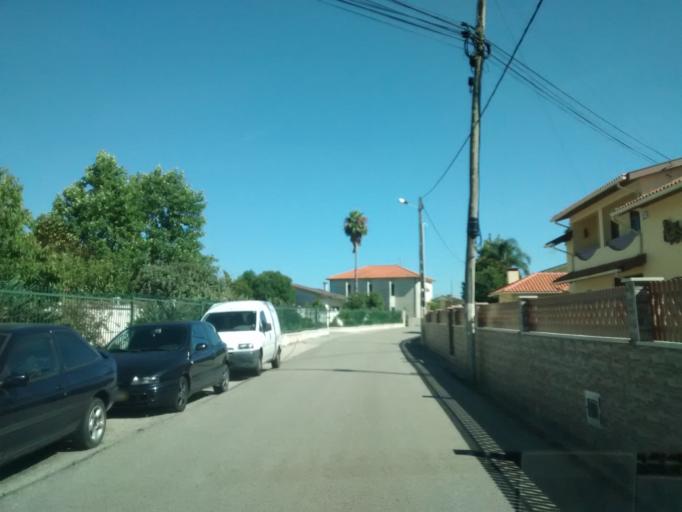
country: PT
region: Aveiro
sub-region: Anadia
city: Sangalhos
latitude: 40.4480
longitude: -8.5061
